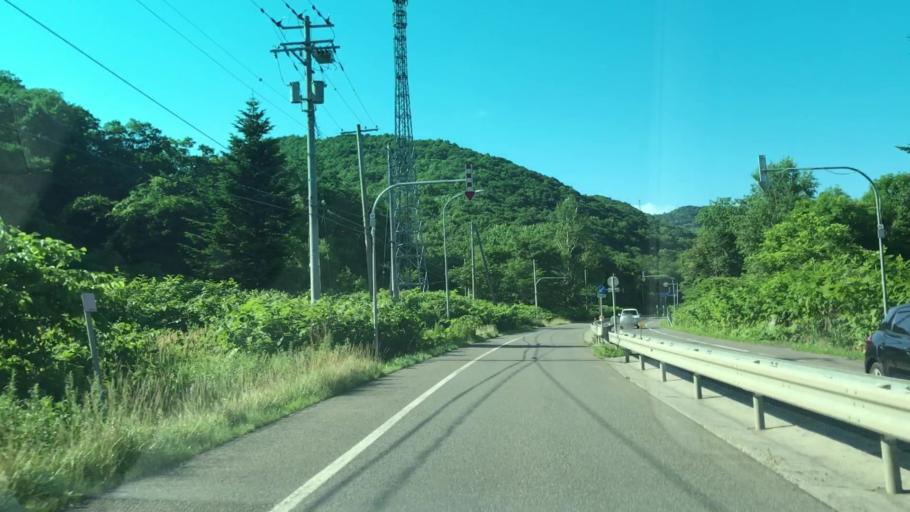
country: JP
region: Hokkaido
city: Iwanai
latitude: 43.0079
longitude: 140.6656
